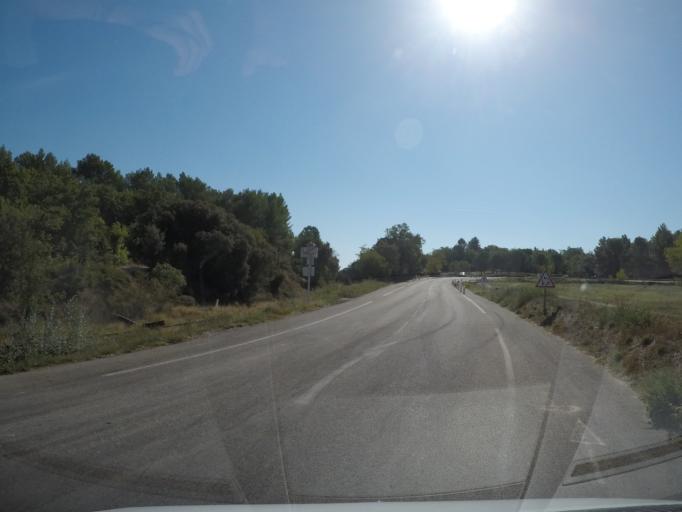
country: FR
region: Languedoc-Roussillon
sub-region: Departement du Gard
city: Castillon-du-Gard
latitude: 43.9578
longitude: 4.5302
